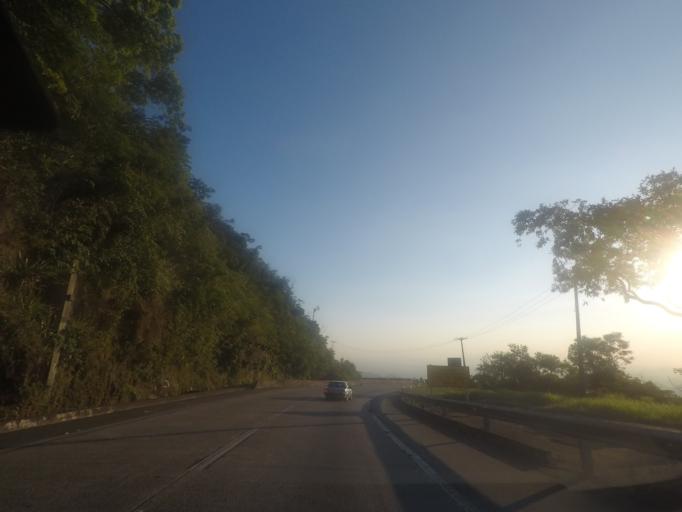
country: BR
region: Rio de Janeiro
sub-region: Petropolis
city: Petropolis
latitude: -22.5290
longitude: -43.2351
